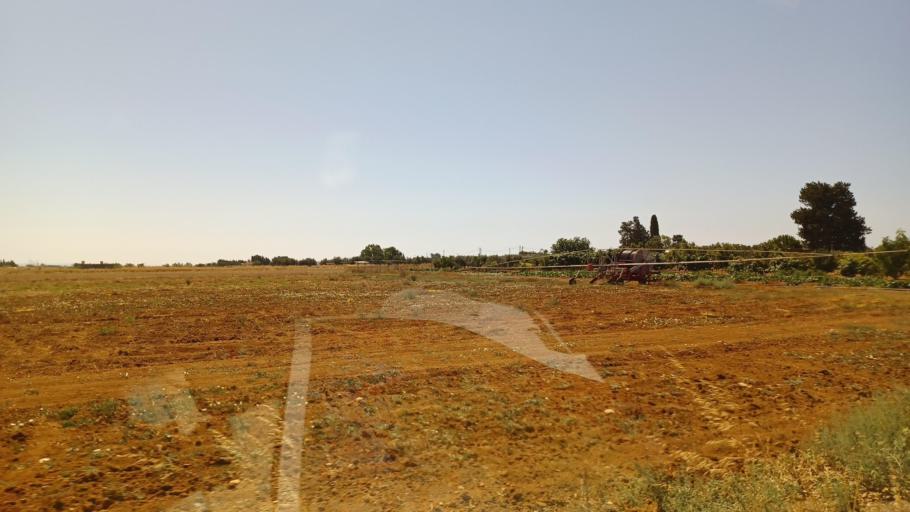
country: CY
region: Larnaka
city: Xylotymbou
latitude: 35.0277
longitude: 33.7307
